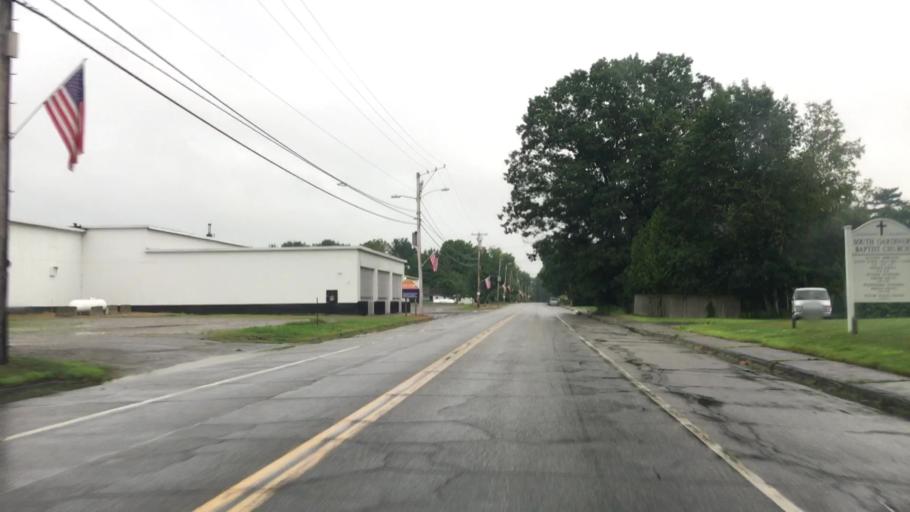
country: US
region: Maine
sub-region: Kennebec County
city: Pittston
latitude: 44.1867
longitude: -69.7571
